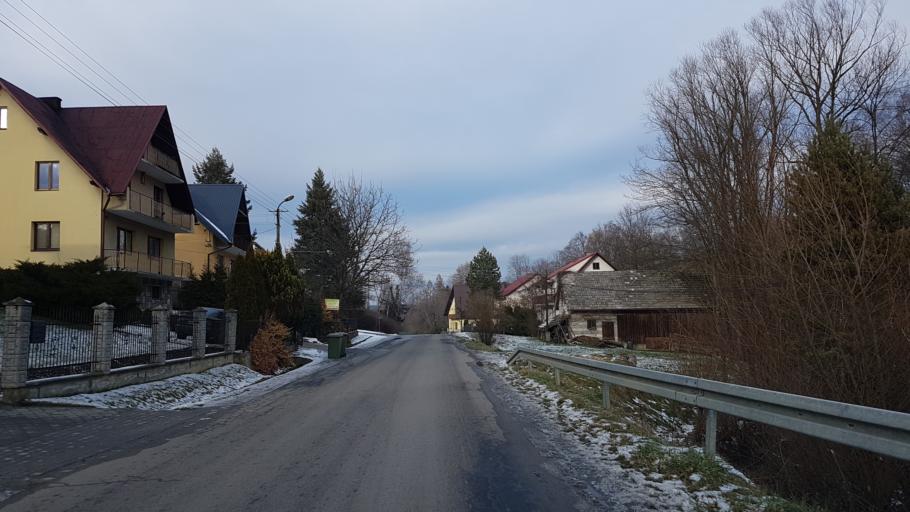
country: PL
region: Lesser Poland Voivodeship
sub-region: Powiat nowosadecki
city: Stary Sacz
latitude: 49.5215
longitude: 20.6087
